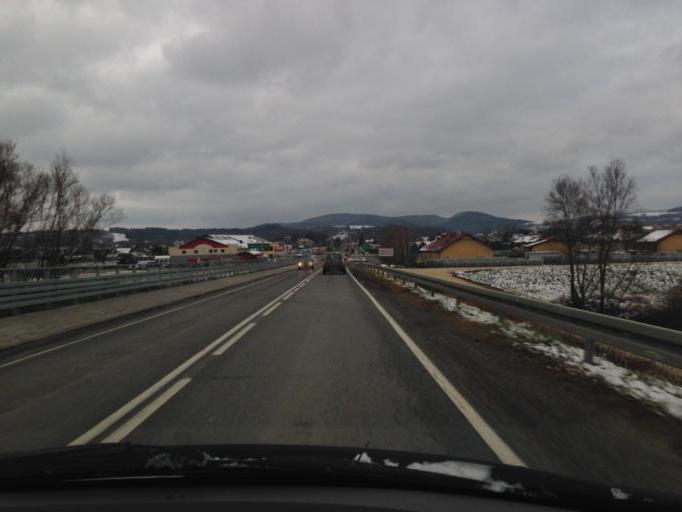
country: PL
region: Lesser Poland Voivodeship
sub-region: Powiat tarnowski
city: Zakliczyn
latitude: 49.8633
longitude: 20.8129
